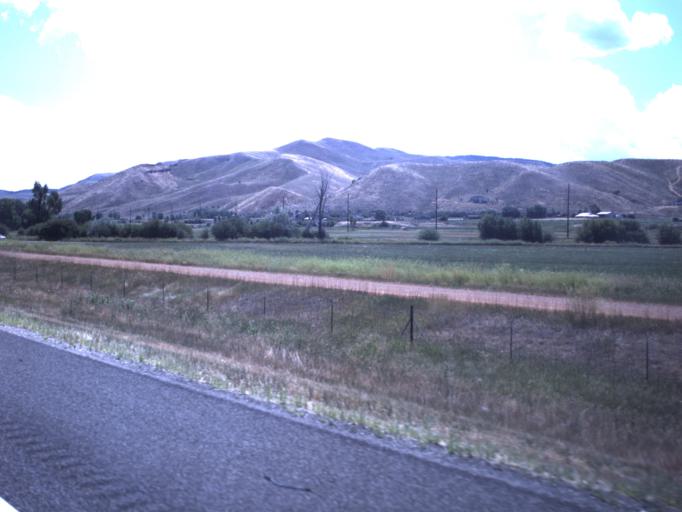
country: US
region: Utah
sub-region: Summit County
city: Coalville
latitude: 41.0091
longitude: -111.4804
